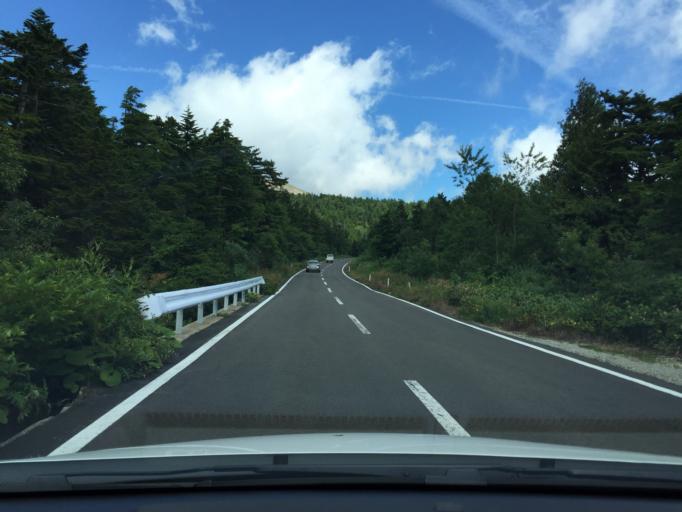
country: JP
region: Fukushima
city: Inawashiro
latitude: 37.7073
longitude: 140.2470
